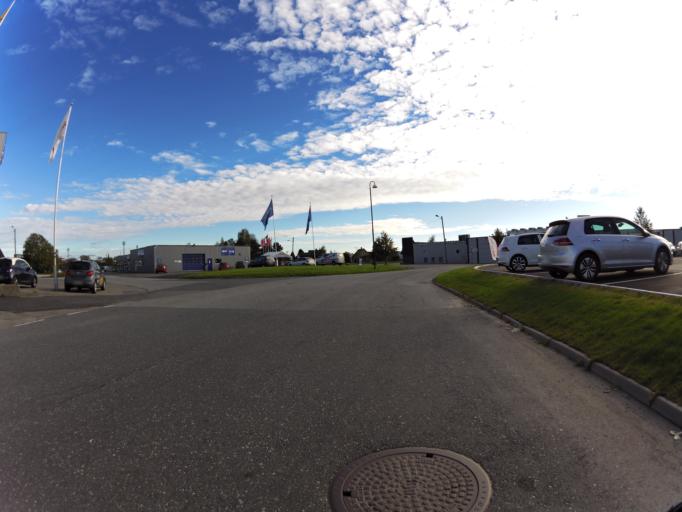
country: NO
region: Ostfold
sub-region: Sarpsborg
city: Sarpsborg
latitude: 59.2878
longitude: 11.0914
